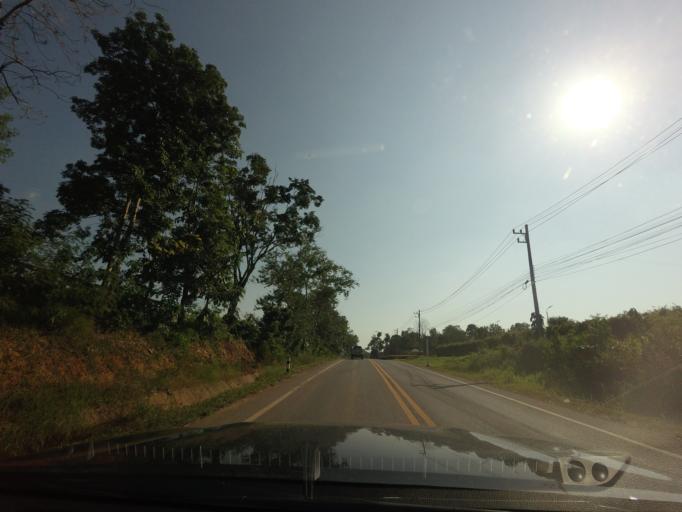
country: TH
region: Nan
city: Nan
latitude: 18.8025
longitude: 100.7999
